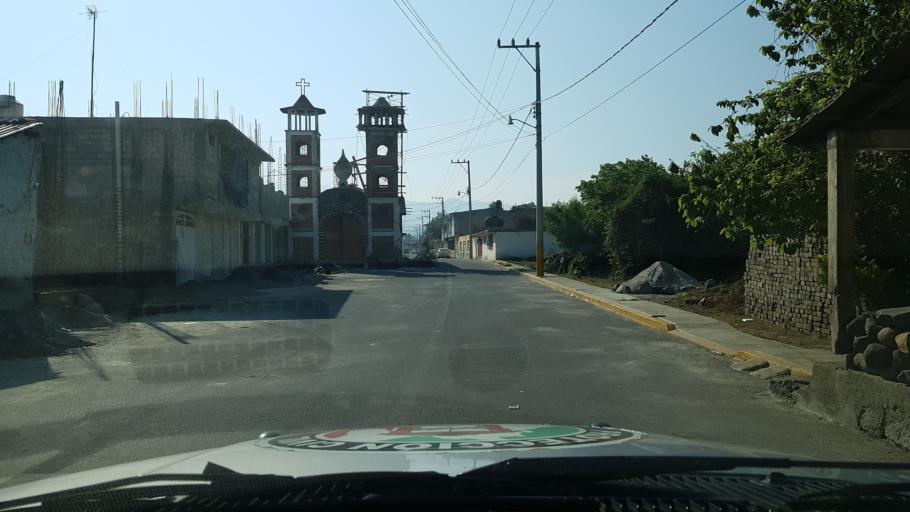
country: MX
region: Mexico
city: Atlautla
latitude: 19.0324
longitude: -98.7800
